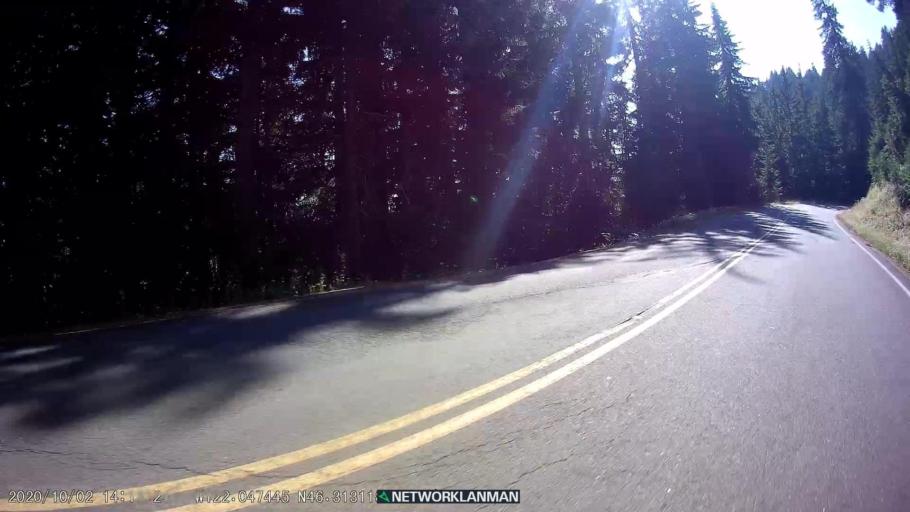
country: US
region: Washington
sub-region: Lewis County
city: Morton
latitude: 46.3124
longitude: -122.0474
